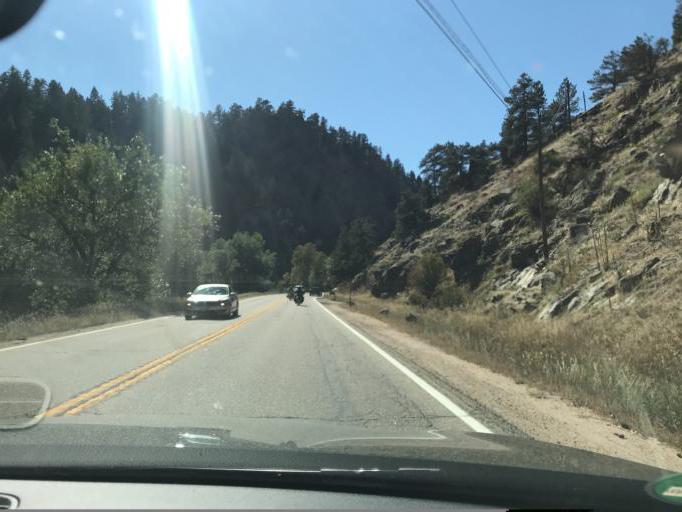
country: US
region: Colorado
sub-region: Boulder County
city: Boulder
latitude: 40.0059
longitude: -105.3425
